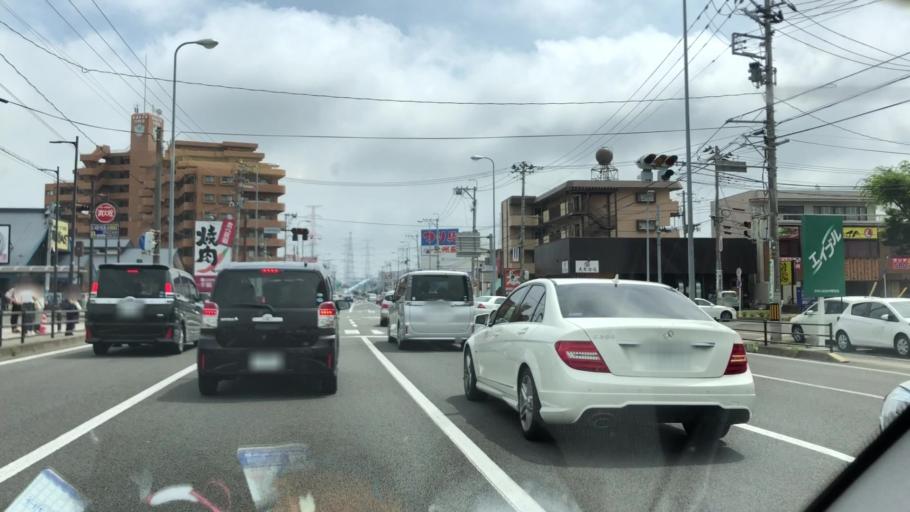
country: JP
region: Miyagi
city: Rifu
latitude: 38.2800
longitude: 140.9848
